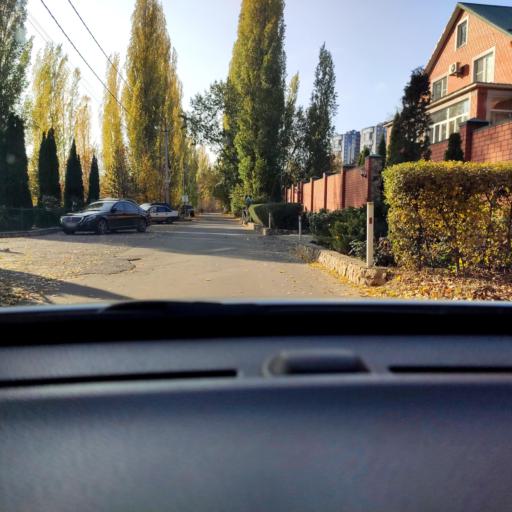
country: RU
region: Voronezj
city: Voronezh
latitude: 51.6987
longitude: 39.2355
